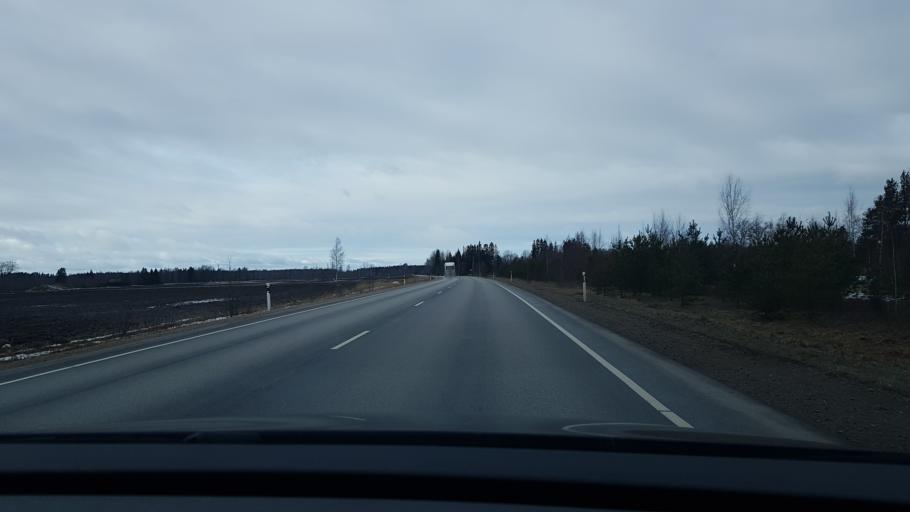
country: EE
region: Paernumaa
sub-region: Paikuse vald
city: Paikuse
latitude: 58.2611
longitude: 24.6676
